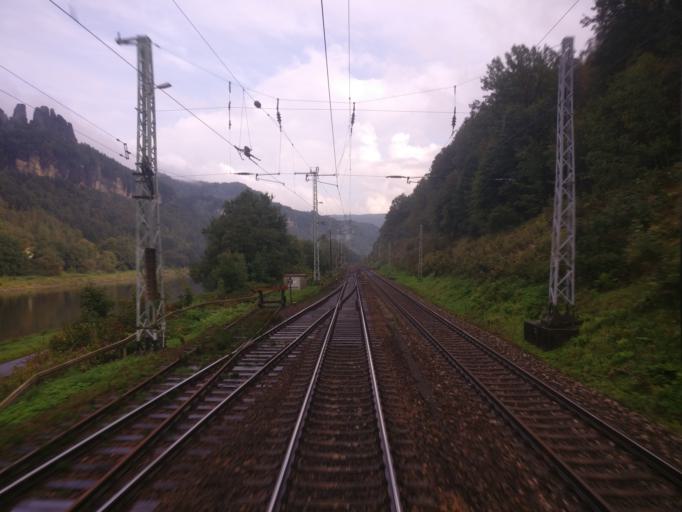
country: DE
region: Saxony
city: Bad Schandau
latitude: 50.9076
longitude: 14.1880
